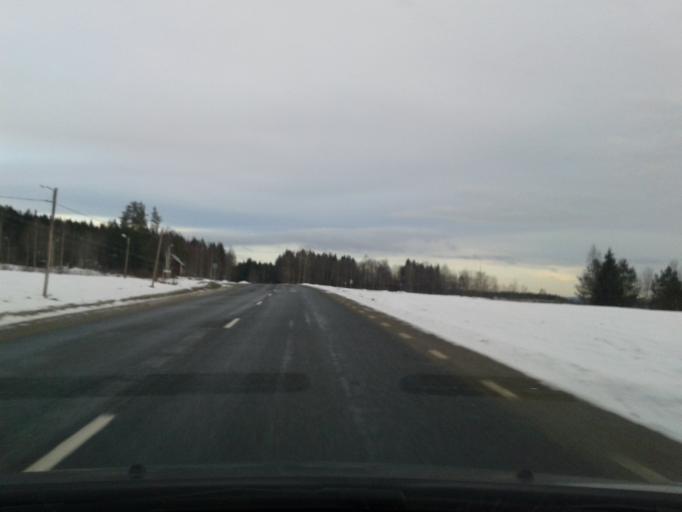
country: SE
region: Vaesternorrland
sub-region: Solleftea Kommun
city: As
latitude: 63.4444
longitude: 16.9131
